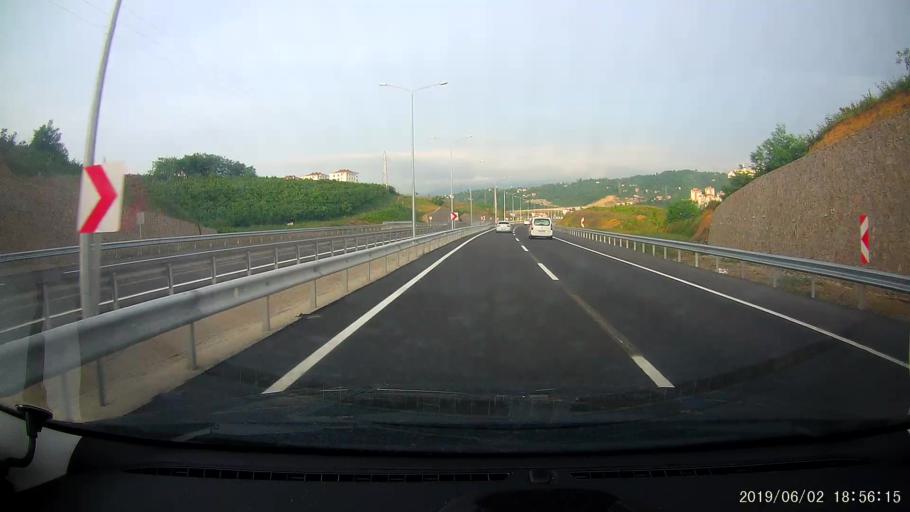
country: TR
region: Ordu
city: Ordu
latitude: 40.9563
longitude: 37.8870
